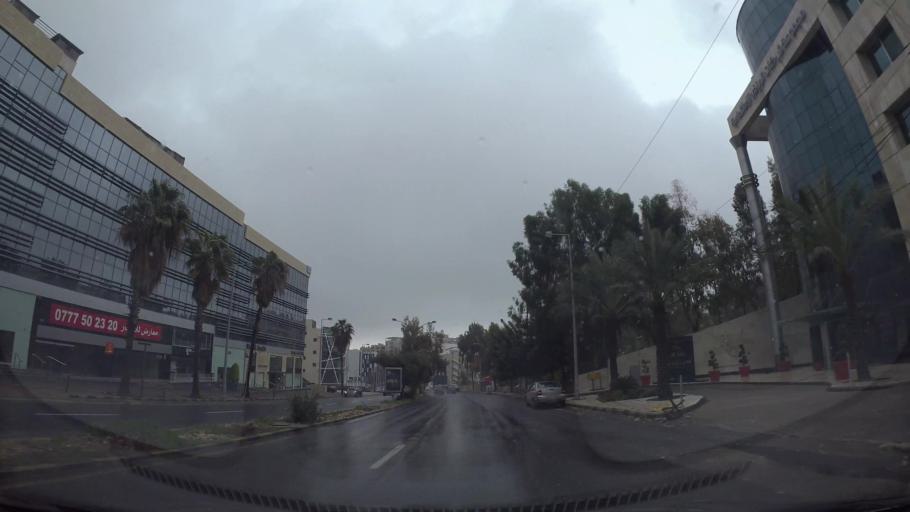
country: JO
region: Amman
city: Amman
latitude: 31.9611
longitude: 35.8914
